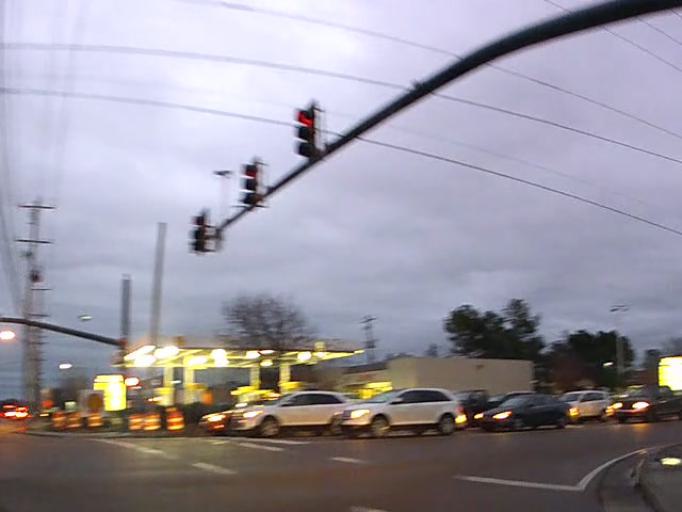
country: US
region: Tennessee
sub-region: Shelby County
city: Collierville
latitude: 35.0458
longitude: -89.6892
